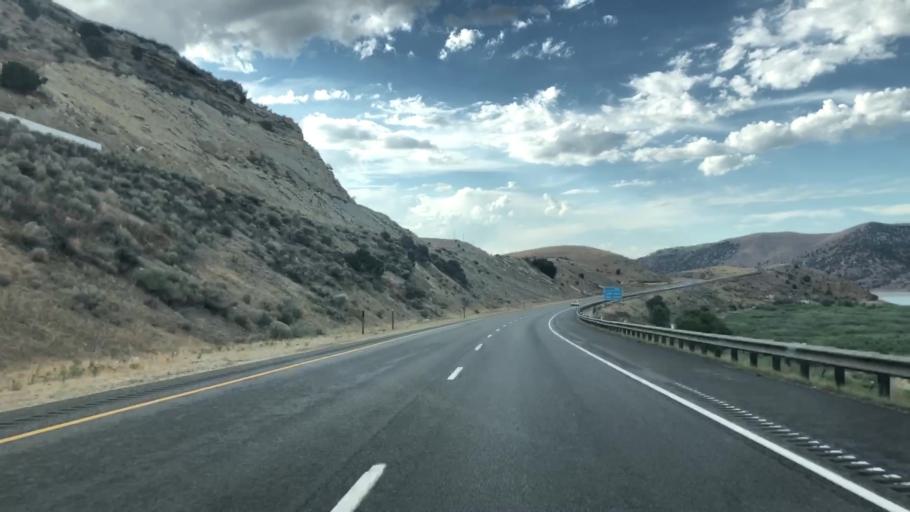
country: US
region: Utah
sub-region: Summit County
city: Coalville
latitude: 40.9392
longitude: -111.4103
